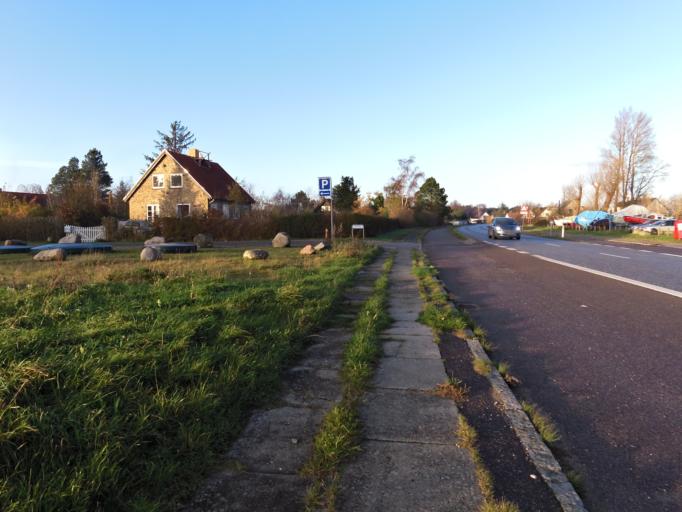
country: DK
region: Central Jutland
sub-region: Arhus Kommune
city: Beder
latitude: 56.0231
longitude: 10.2607
